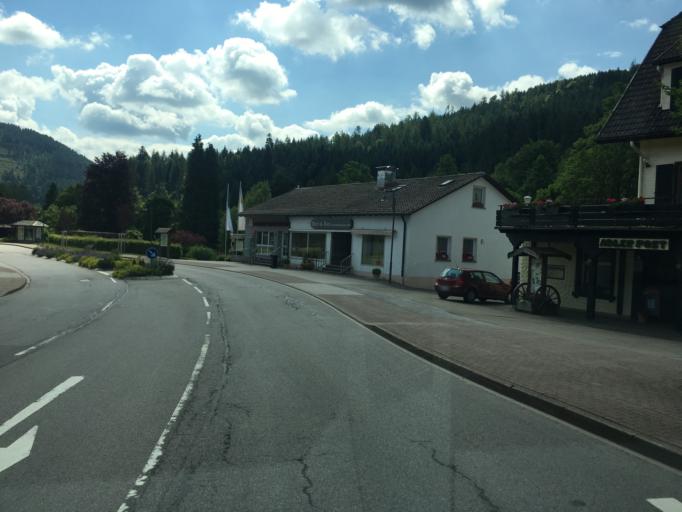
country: DE
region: Baden-Wuerttemberg
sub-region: Karlsruhe Region
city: Biberach
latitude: 48.5331
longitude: 8.2889
